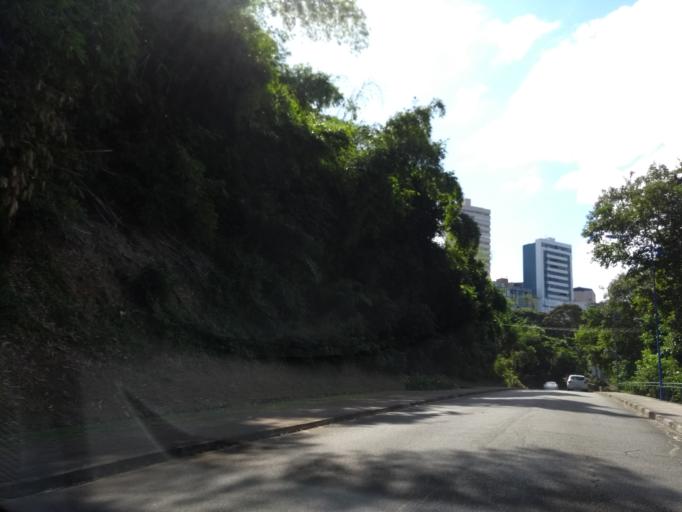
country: BR
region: Bahia
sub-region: Salvador
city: Salvador
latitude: -13.0033
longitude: -38.5105
